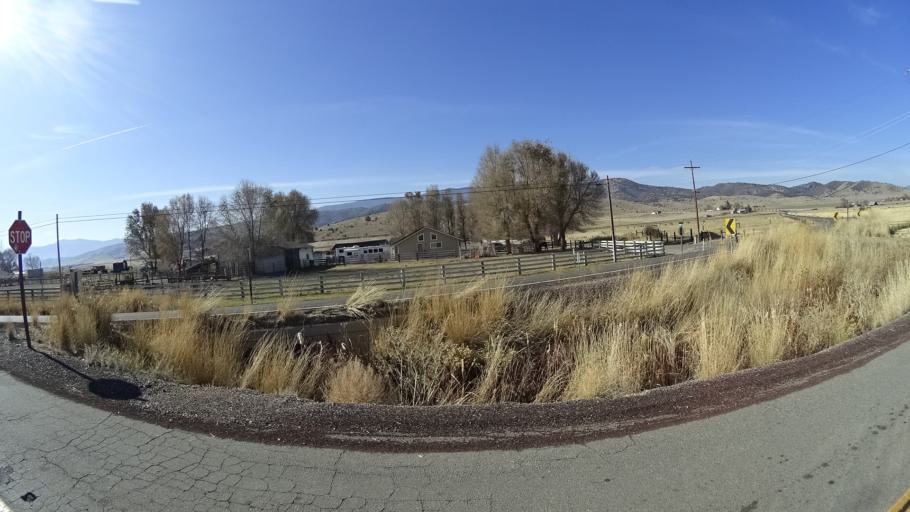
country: US
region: California
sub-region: Siskiyou County
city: Montague
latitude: 41.6033
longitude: -122.5235
